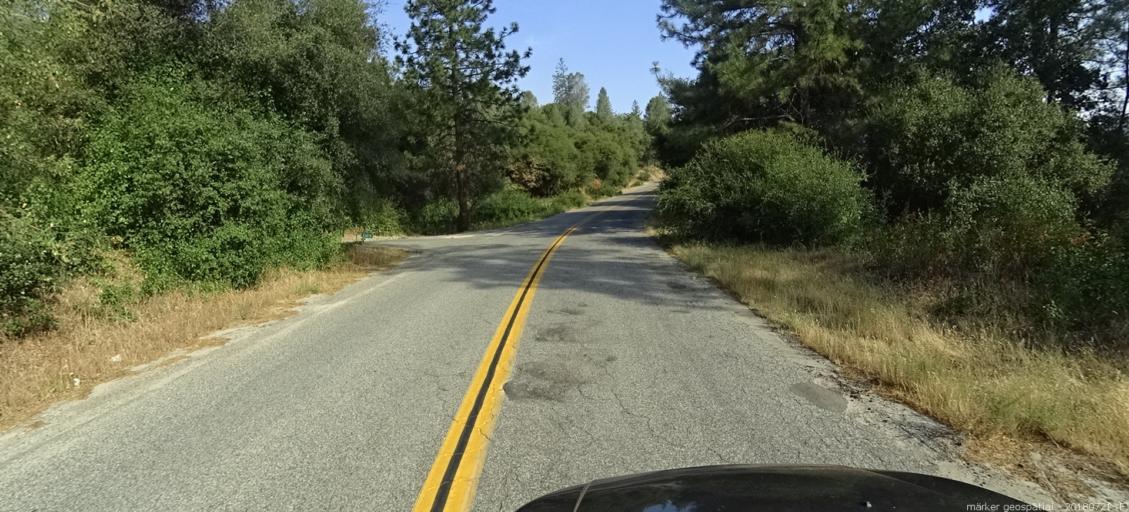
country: US
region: California
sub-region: Fresno County
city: Auberry
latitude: 37.2348
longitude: -119.5156
